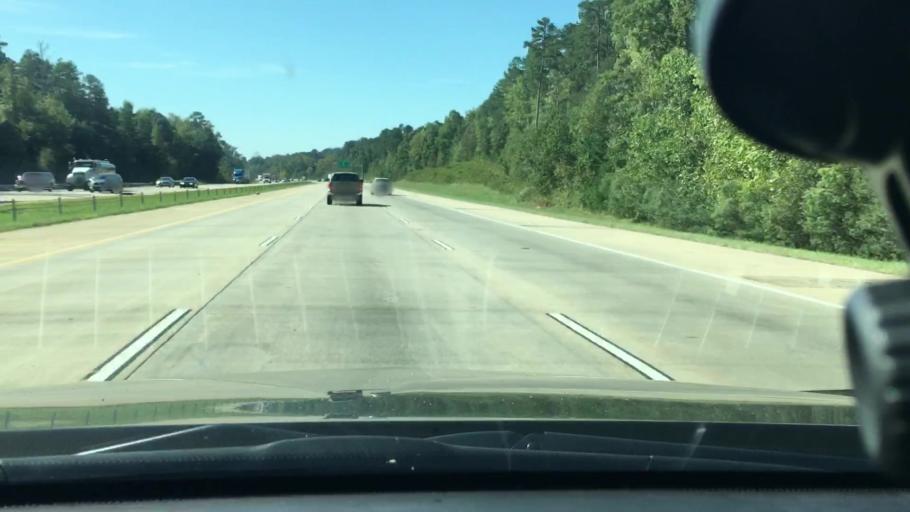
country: US
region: North Carolina
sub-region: Gaston County
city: Mount Holly
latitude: 35.3106
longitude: -80.9507
